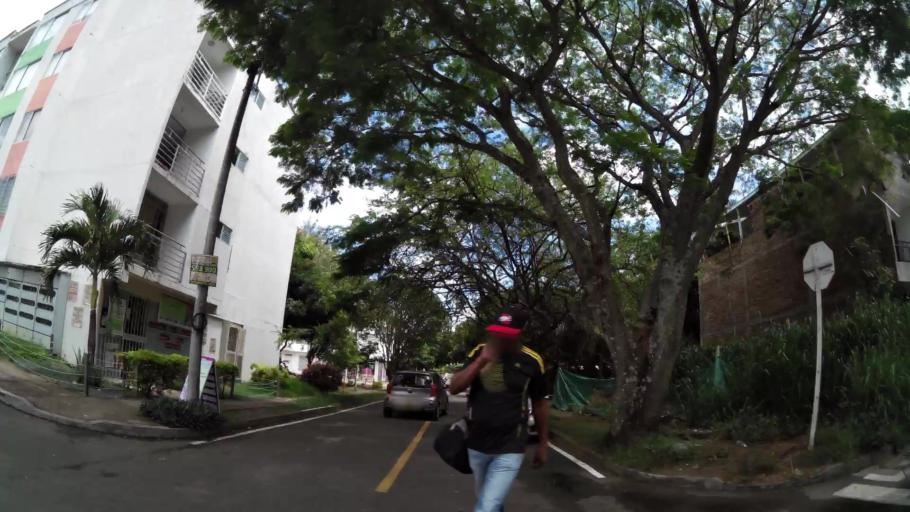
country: CO
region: Valle del Cauca
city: Cali
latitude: 3.3829
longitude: -76.5157
